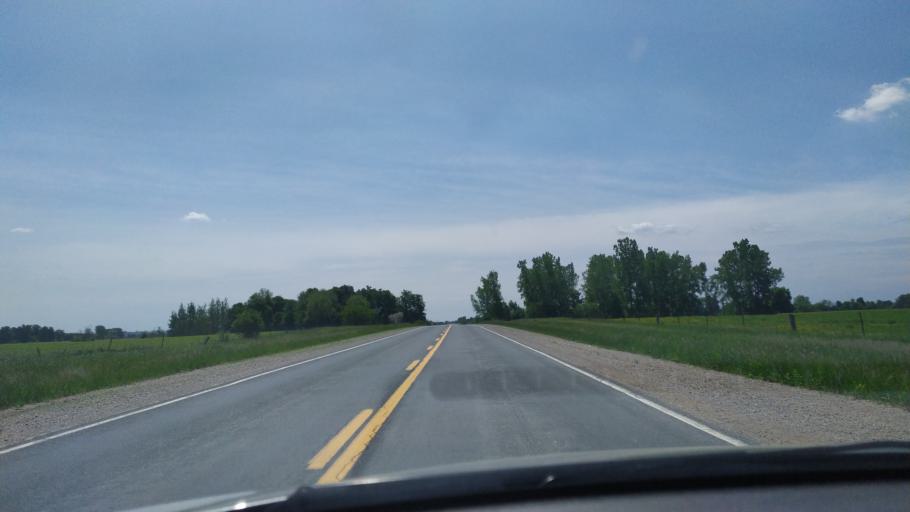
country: CA
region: Ontario
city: Ingersoll
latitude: 43.0254
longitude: -80.9705
